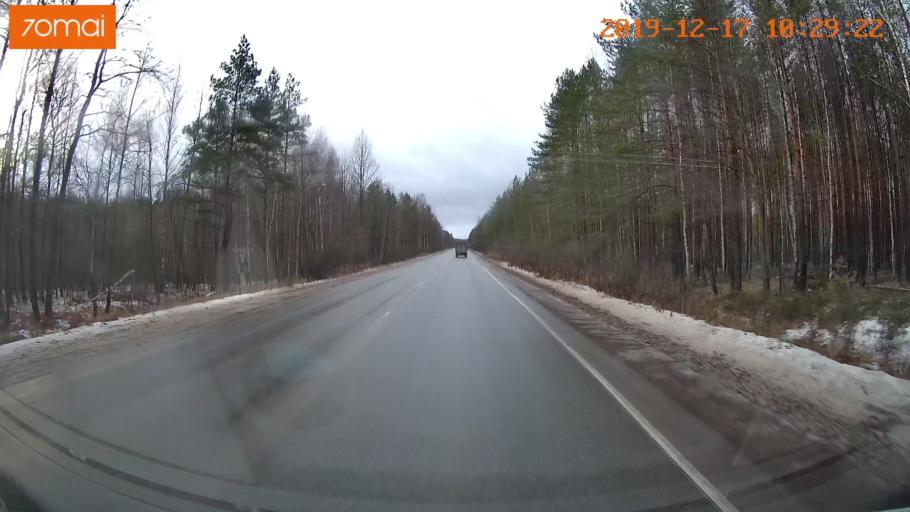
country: RU
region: Vladimir
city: Anopino
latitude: 55.6529
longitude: 40.7215
